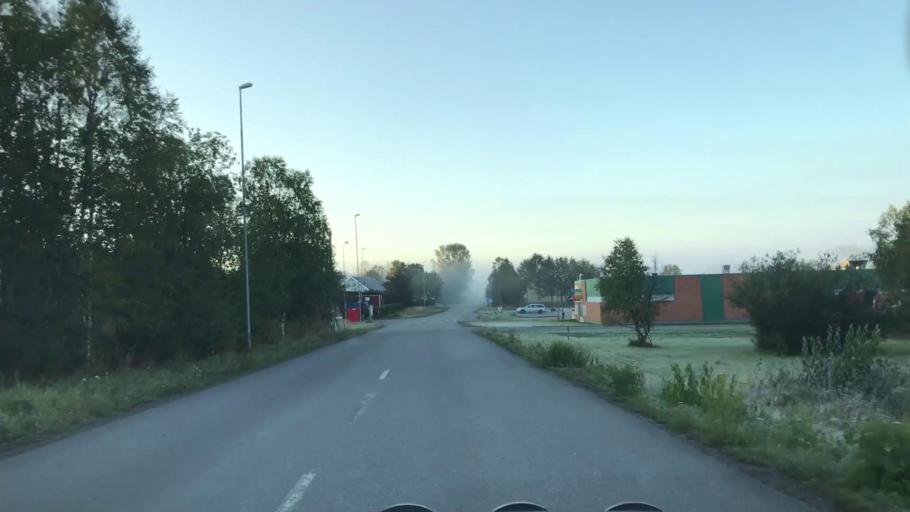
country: SE
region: Norrbotten
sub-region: Gallivare Kommun
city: Malmberget
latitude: 67.6493
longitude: 21.0455
